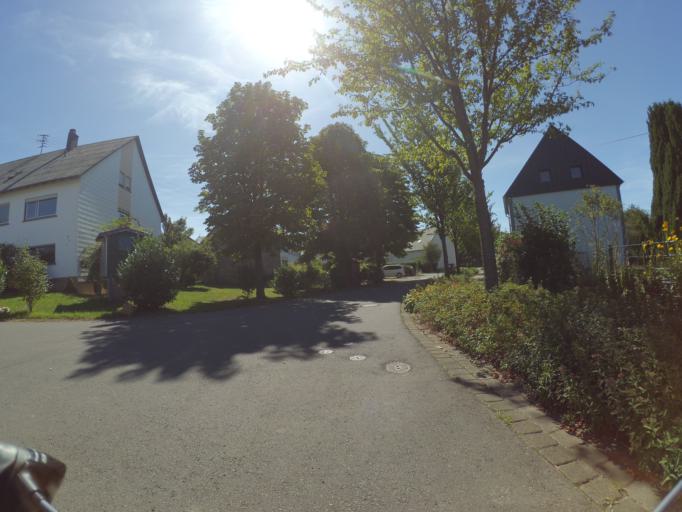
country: DE
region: Rheinland-Pfalz
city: Morbach
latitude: 49.8072
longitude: 7.0733
